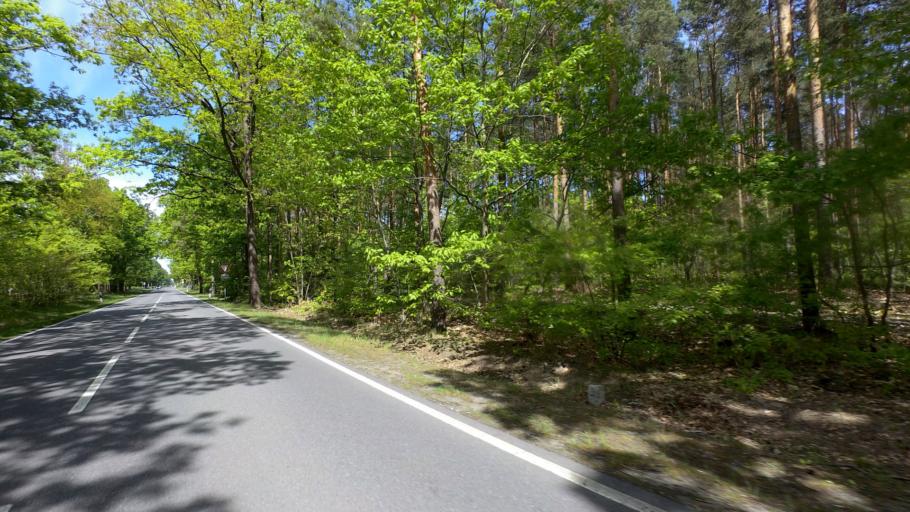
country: DE
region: Brandenburg
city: Sperenberg
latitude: 52.0982
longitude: 13.3747
